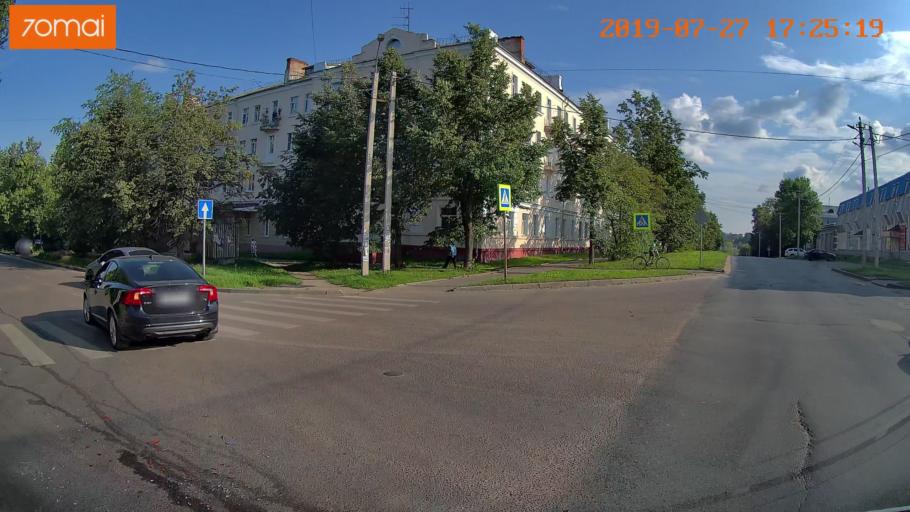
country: RU
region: Ivanovo
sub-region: Gorod Ivanovo
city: Ivanovo
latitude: 57.0176
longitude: 40.9577
